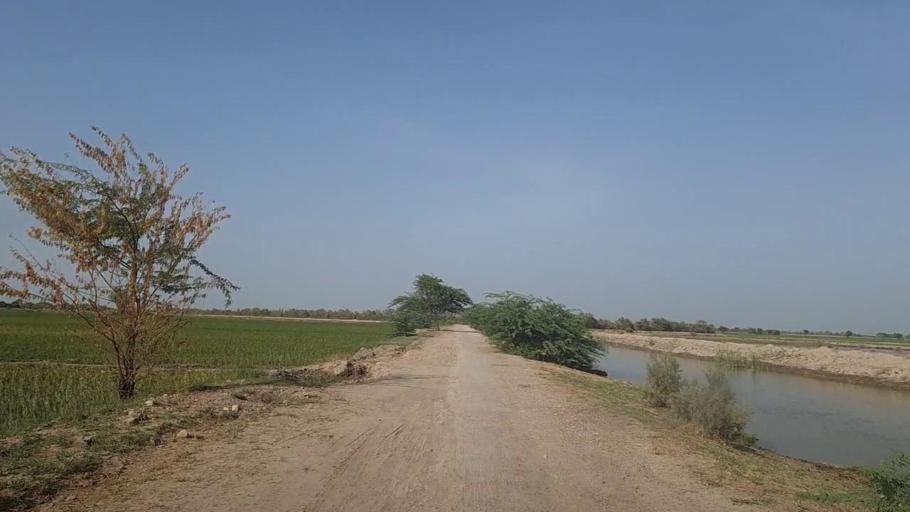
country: PK
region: Sindh
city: Sita Road
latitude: 27.0953
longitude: 67.8711
